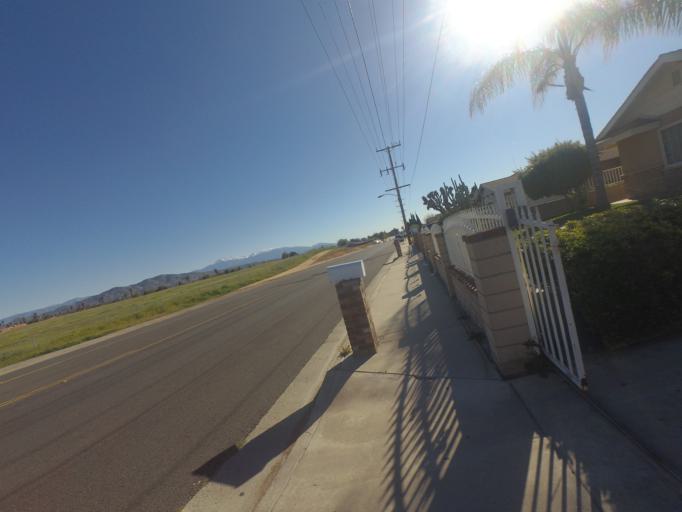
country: US
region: California
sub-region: Riverside County
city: March Air Force Base
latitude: 33.9244
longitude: -117.2683
